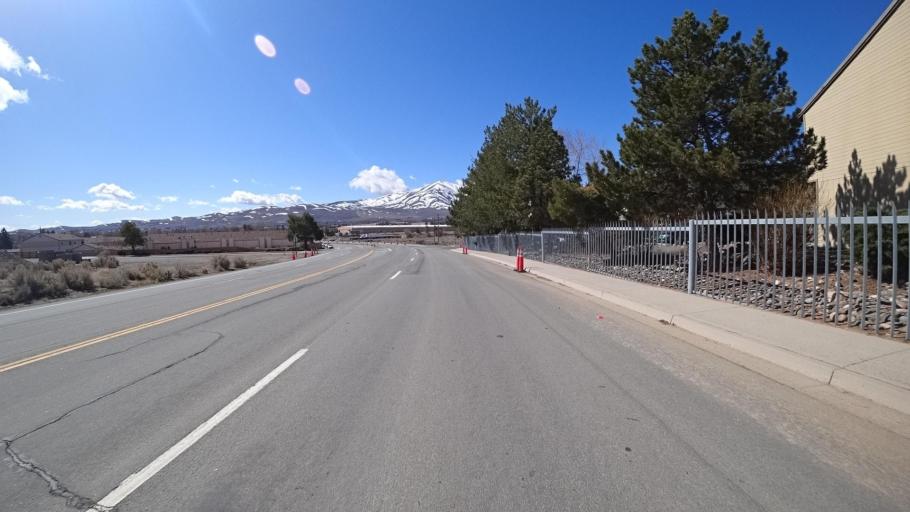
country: US
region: Nevada
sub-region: Washoe County
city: Lemmon Valley
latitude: 39.6455
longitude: -119.8808
